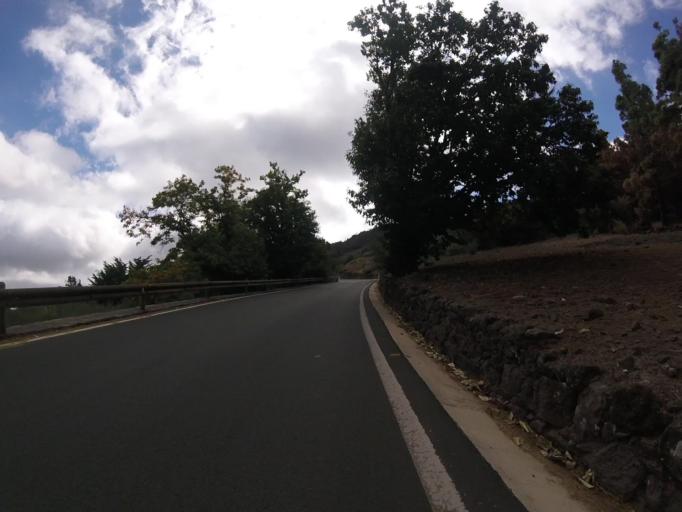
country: ES
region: Canary Islands
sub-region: Provincia de Las Palmas
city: San Bartolome
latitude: 27.9717
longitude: -15.5732
